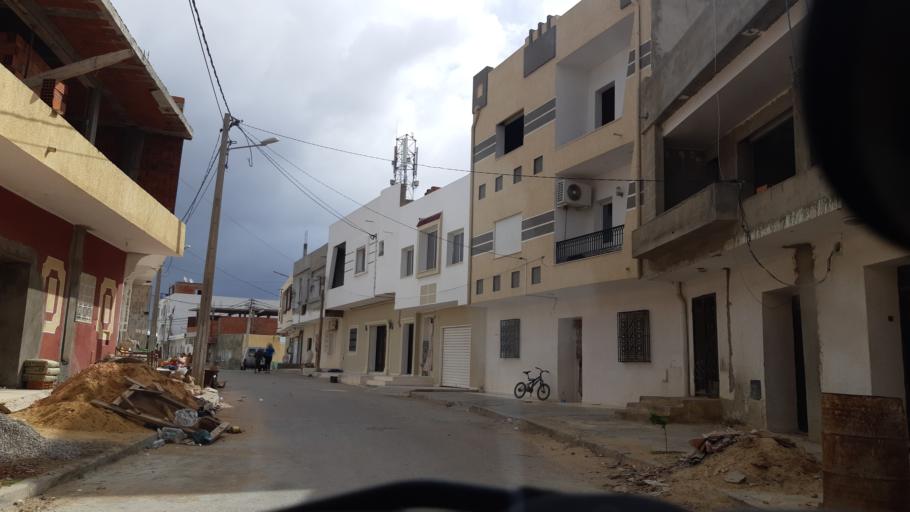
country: TN
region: Susah
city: Akouda
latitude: 35.8685
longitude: 10.5246
